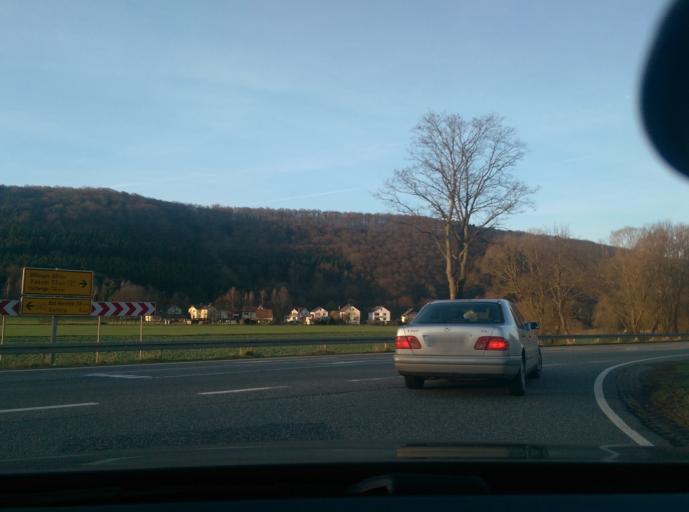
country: DE
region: Hesse
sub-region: Regierungsbezirk Kassel
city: Sontra
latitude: 51.1023
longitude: 9.9662
